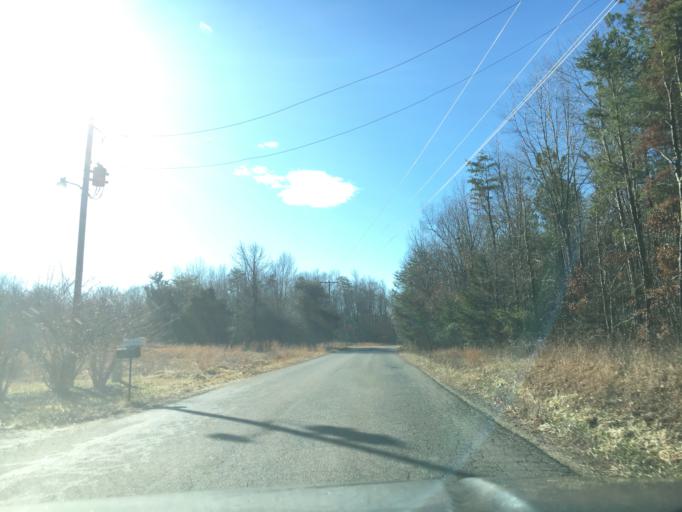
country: US
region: Virginia
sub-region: Fauquier County
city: Bealeton
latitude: 38.4766
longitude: -77.6501
